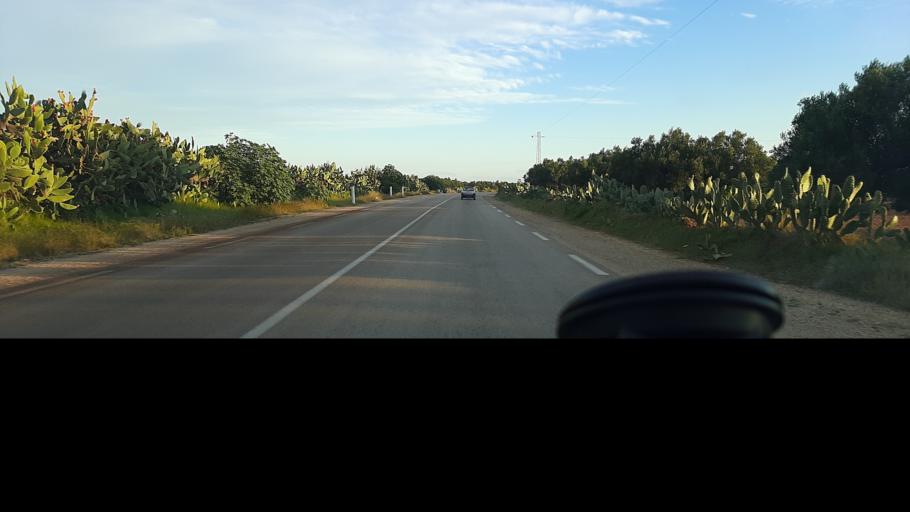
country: TN
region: Safaqis
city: Sfax
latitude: 34.9306
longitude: 10.6214
